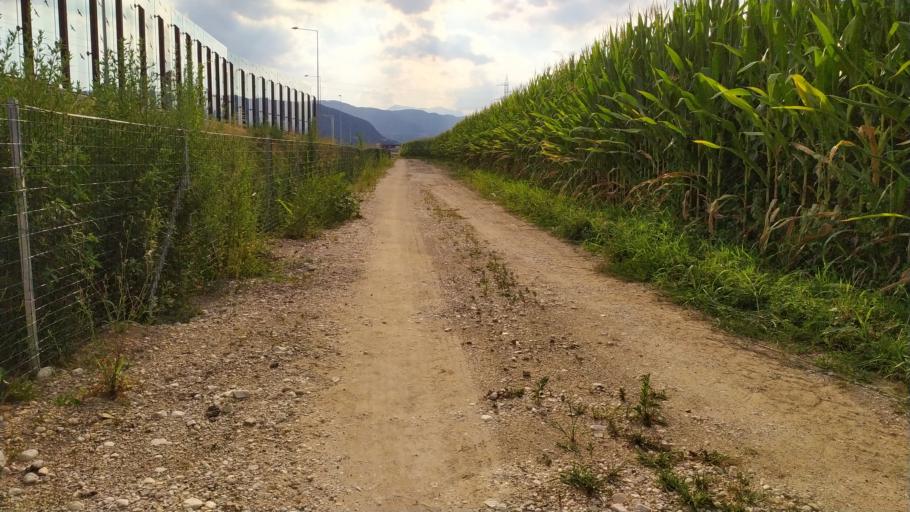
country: IT
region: Veneto
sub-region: Provincia di Vicenza
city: Isola Vicentina
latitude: 45.6490
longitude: 11.4510
